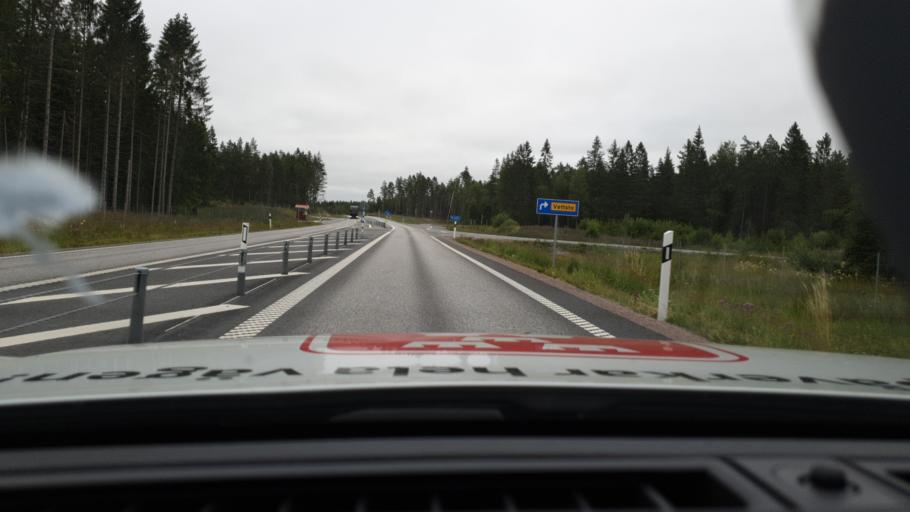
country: SE
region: Uppsala
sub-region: Osthammars Kommun
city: Gimo
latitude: 60.1221
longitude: 18.1472
